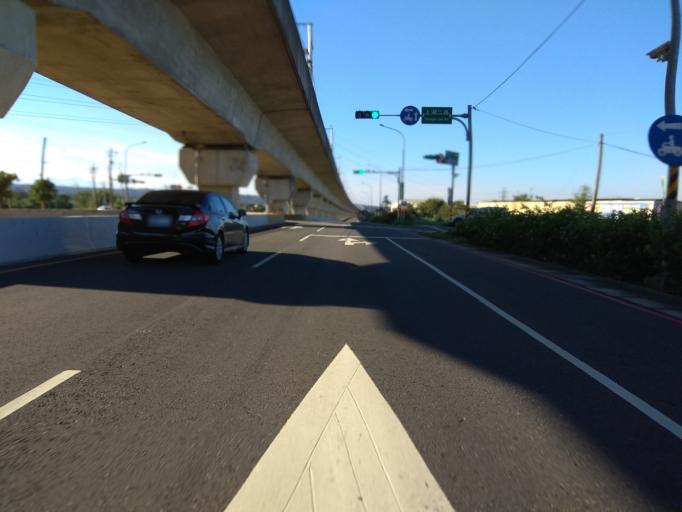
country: TW
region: Taiwan
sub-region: Hsinchu
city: Zhubei
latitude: 24.9076
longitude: 121.0862
